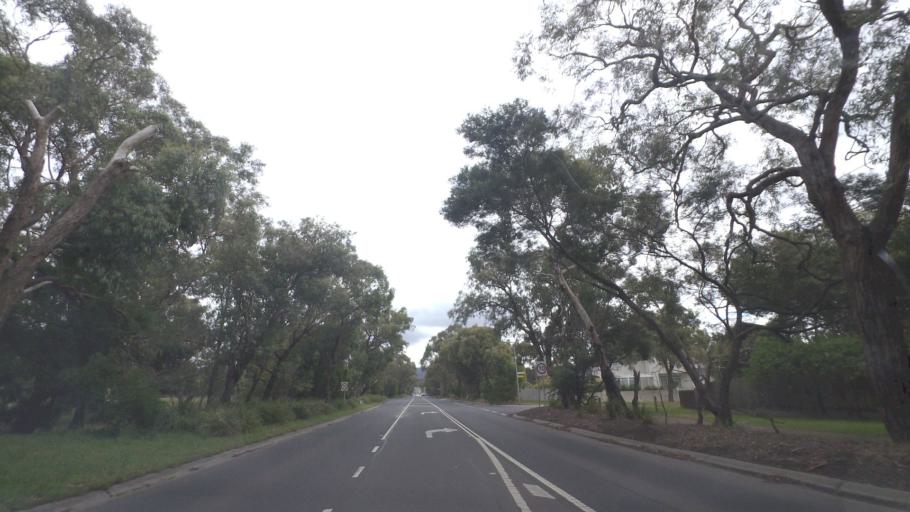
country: AU
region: Victoria
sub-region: Maroondah
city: Kilsyth South
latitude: -37.8231
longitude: 145.3175
